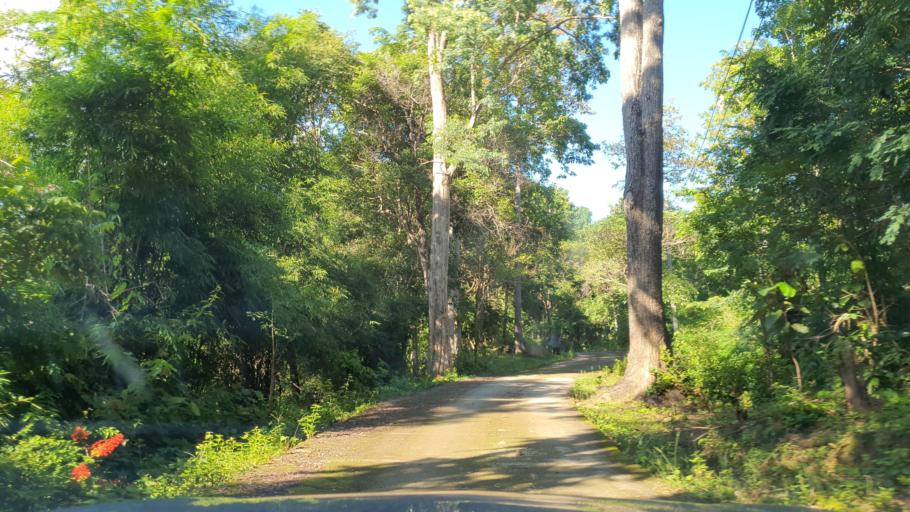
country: TH
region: Chiang Mai
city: Mae On
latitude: 18.8124
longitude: 99.3159
